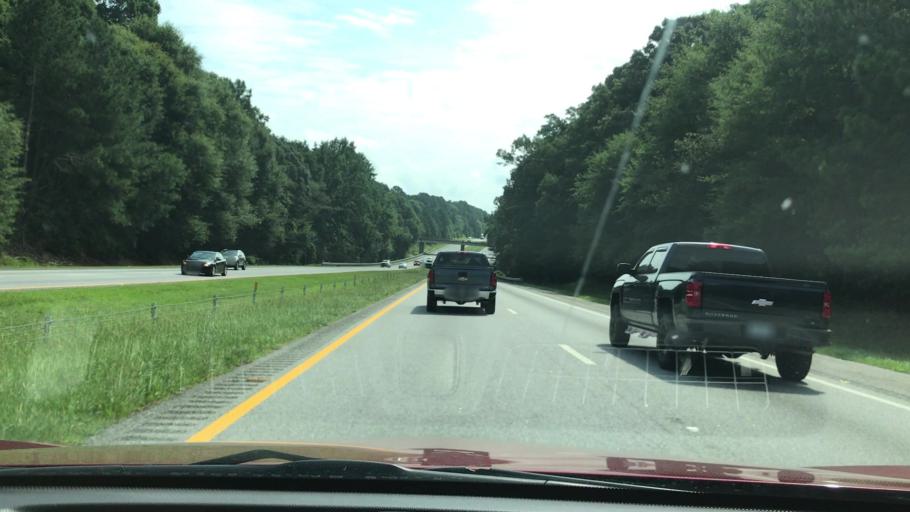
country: US
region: Georgia
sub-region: Hart County
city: Reed Creek
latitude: 34.5096
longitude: -82.9501
